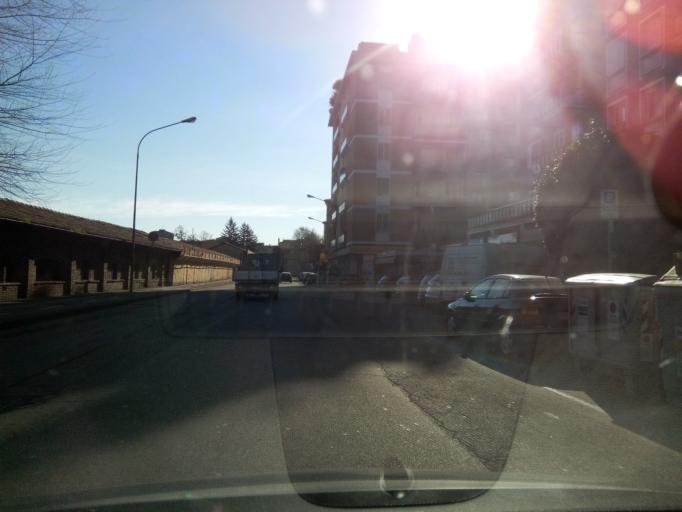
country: IT
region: Emilia-Romagna
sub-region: Provincia di Bologna
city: Bologna
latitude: 44.4970
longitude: 11.3239
